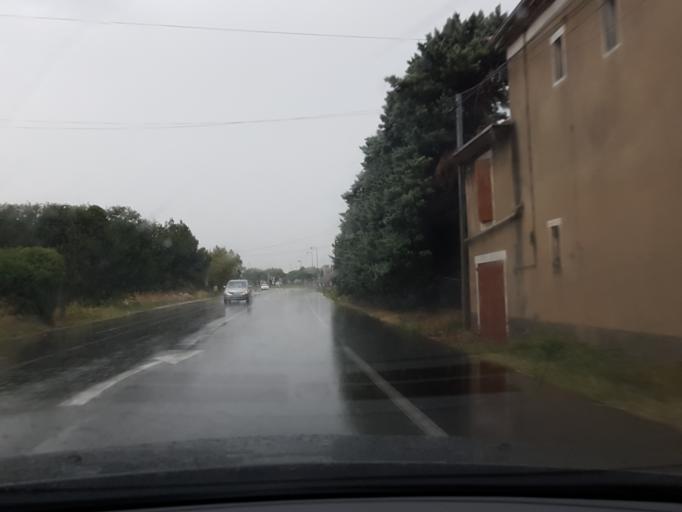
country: FR
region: Provence-Alpes-Cote d'Azur
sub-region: Departement du Vaucluse
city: Carpentras
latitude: 44.0314
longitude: 5.0385
